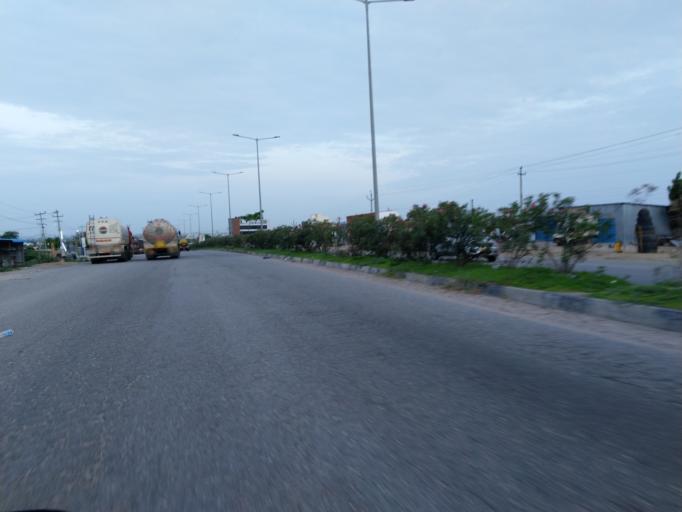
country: IN
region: Telangana
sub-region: Rangareddi
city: Lal Bahadur Nagar
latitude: 17.3174
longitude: 78.6641
